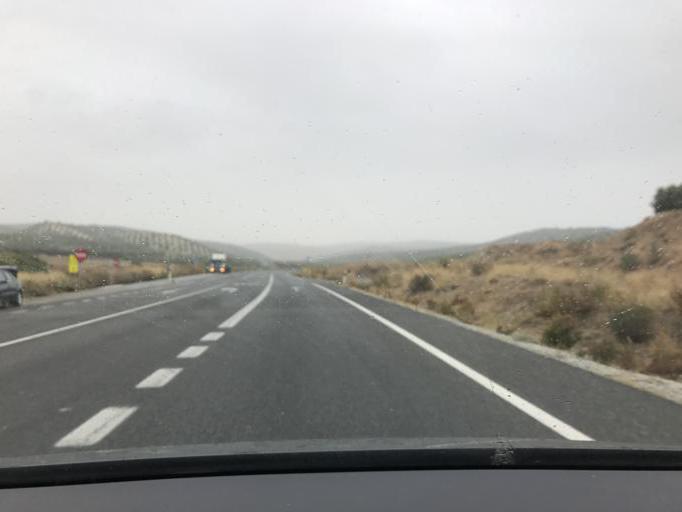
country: ES
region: Andalusia
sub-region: Provincia de Granada
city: Las Gabias
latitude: 37.1605
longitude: -3.7255
